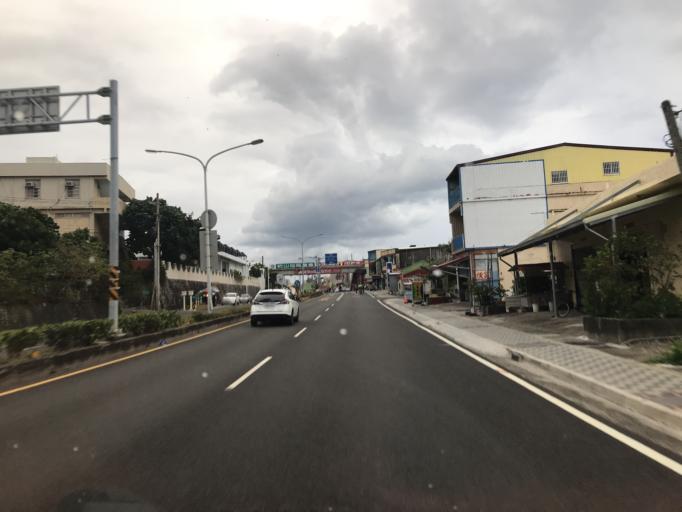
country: TW
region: Taiwan
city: Hengchun
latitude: 22.1925
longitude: 120.6918
